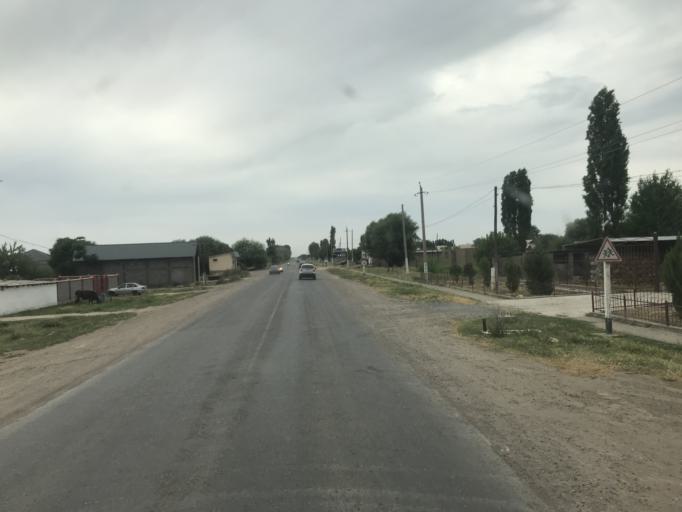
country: KZ
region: Ongtustik Qazaqstan
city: Asykata
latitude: 40.9029
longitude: 68.3569
